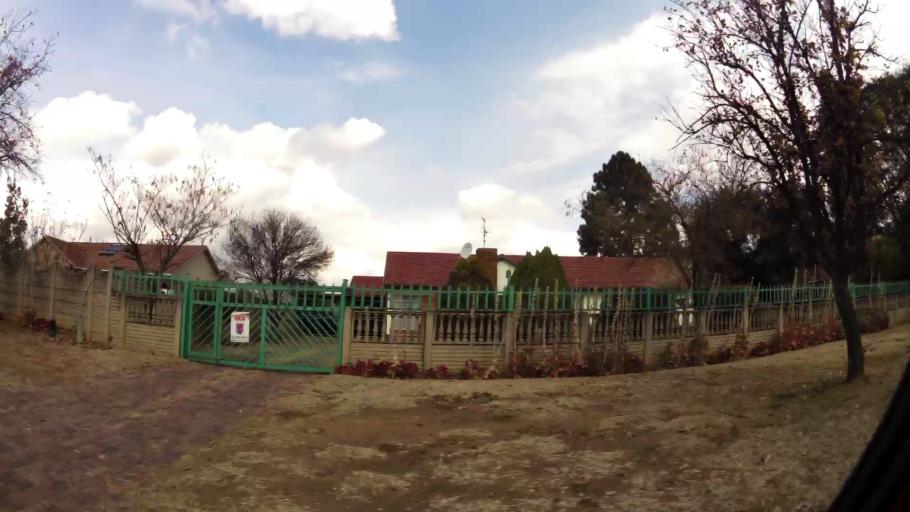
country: ZA
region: Gauteng
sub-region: Sedibeng District Municipality
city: Vanderbijlpark
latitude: -26.7176
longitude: 27.8571
